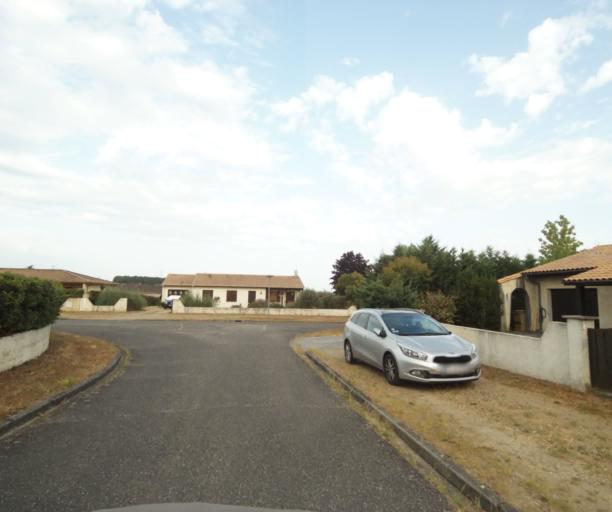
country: FR
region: Aquitaine
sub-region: Departement de la Gironde
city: Creon
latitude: 44.7725
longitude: -0.3556
